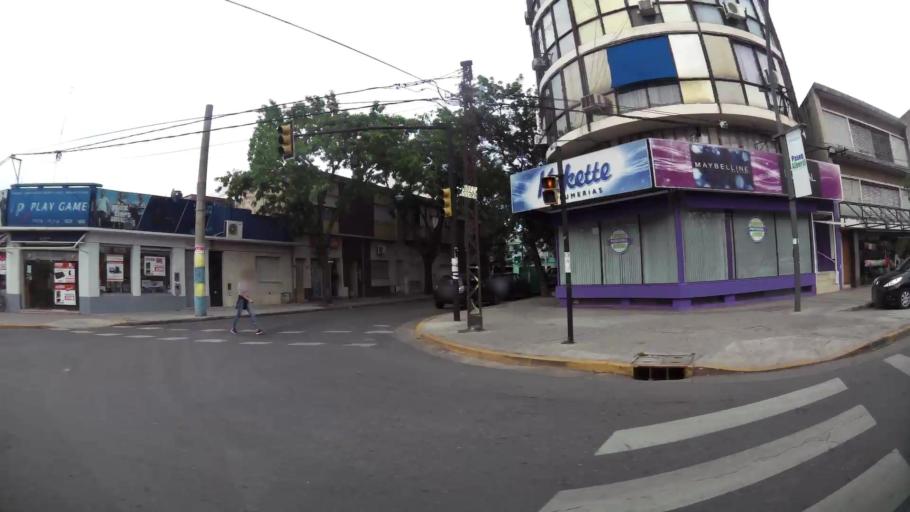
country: AR
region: Santa Fe
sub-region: Departamento de Rosario
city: Rosario
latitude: -32.9164
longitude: -60.6846
